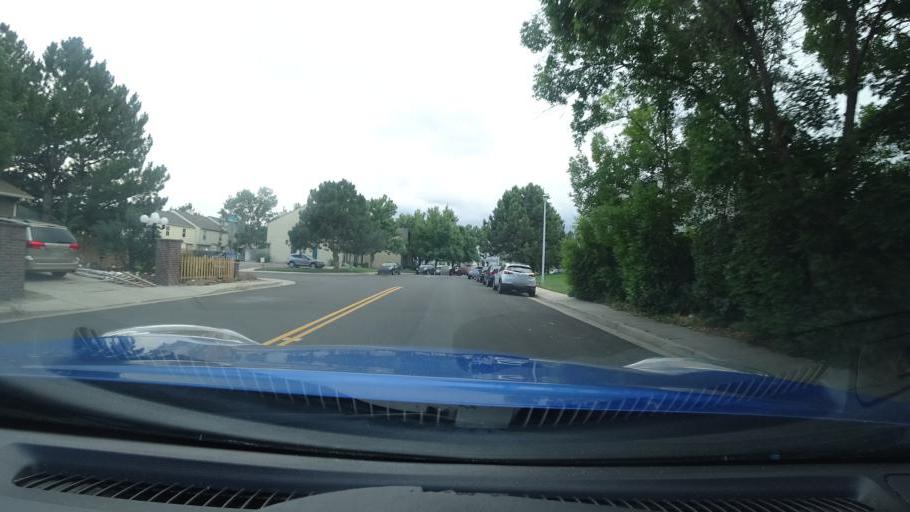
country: US
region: Colorado
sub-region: Adams County
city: Aurora
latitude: 39.6877
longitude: -104.8069
